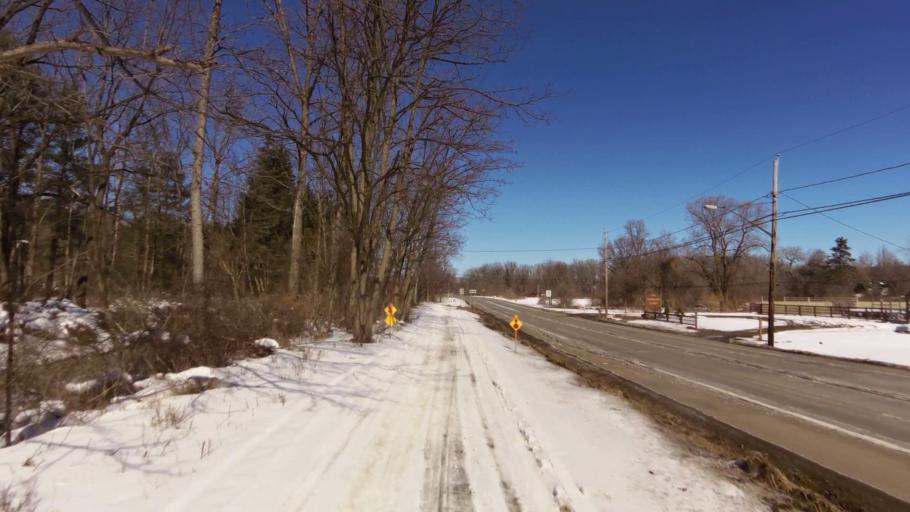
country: US
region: New York
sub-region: Allegany County
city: Houghton
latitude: 42.3693
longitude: -78.1396
